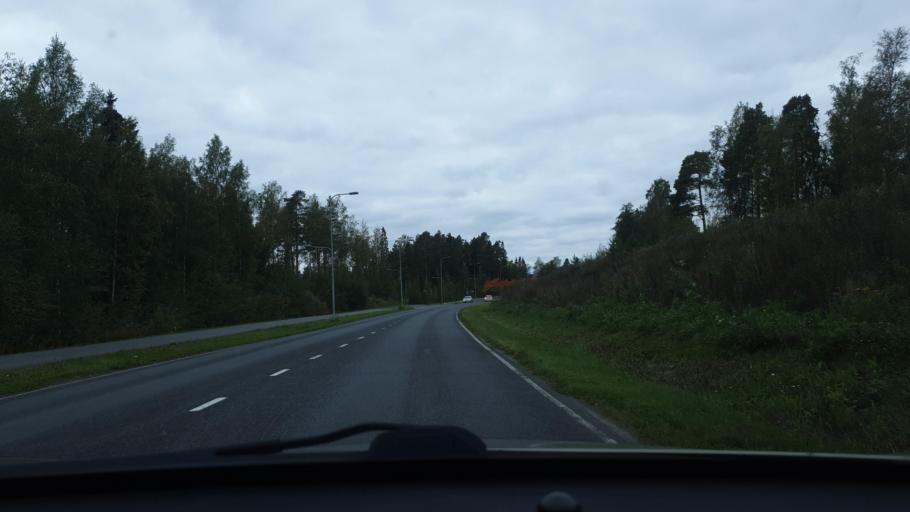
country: FI
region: Ostrobothnia
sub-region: Vaasa
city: Korsholm
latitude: 63.1021
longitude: 21.6840
